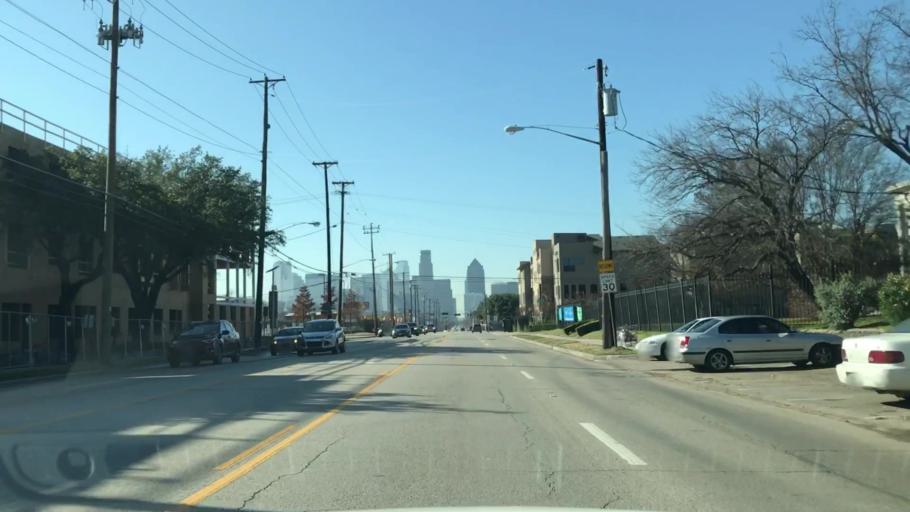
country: US
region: Texas
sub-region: Dallas County
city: Highland Park
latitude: 32.8045
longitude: -96.7782
